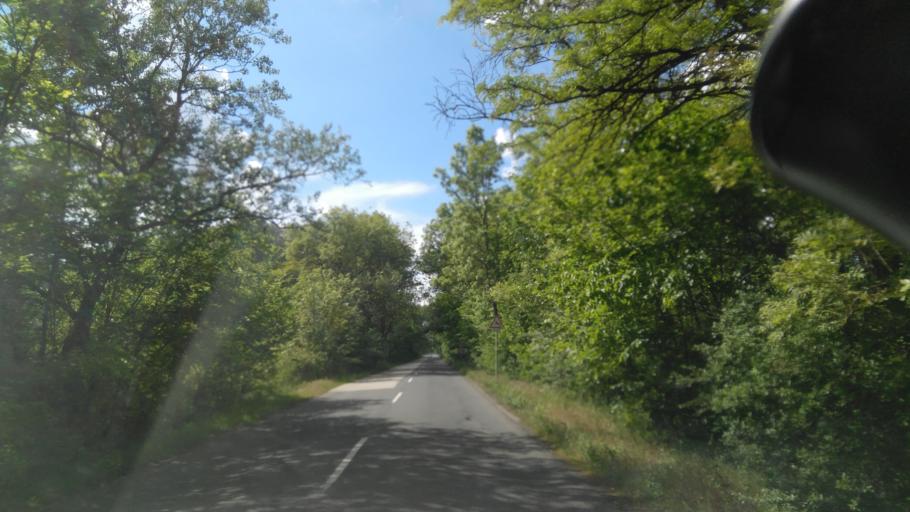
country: HU
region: Bekes
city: Bucsa
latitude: 47.1771
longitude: 21.0591
